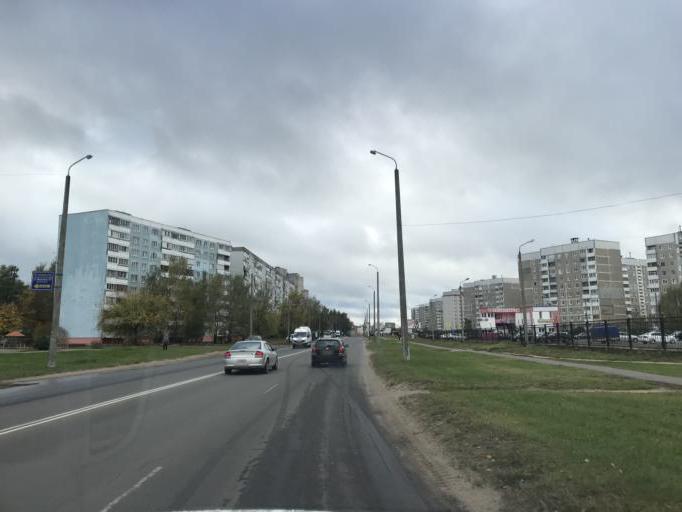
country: BY
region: Mogilev
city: Mahilyow
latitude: 53.8791
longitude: 30.3691
